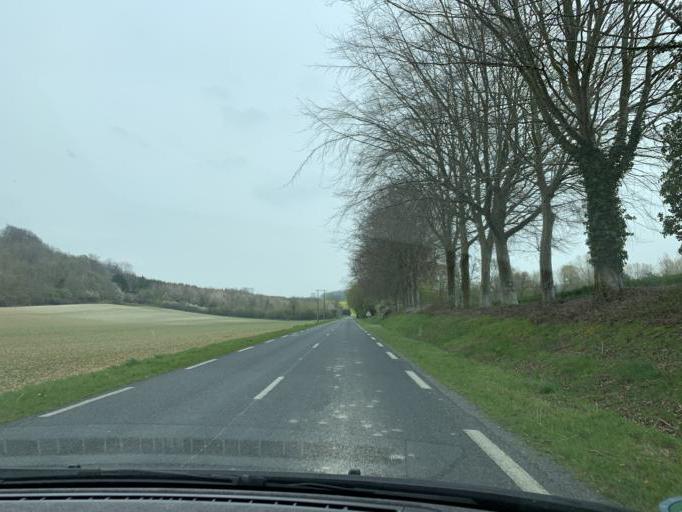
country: FR
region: Haute-Normandie
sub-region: Departement de la Seine-Maritime
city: Londinieres
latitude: 49.8408
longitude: 1.4416
